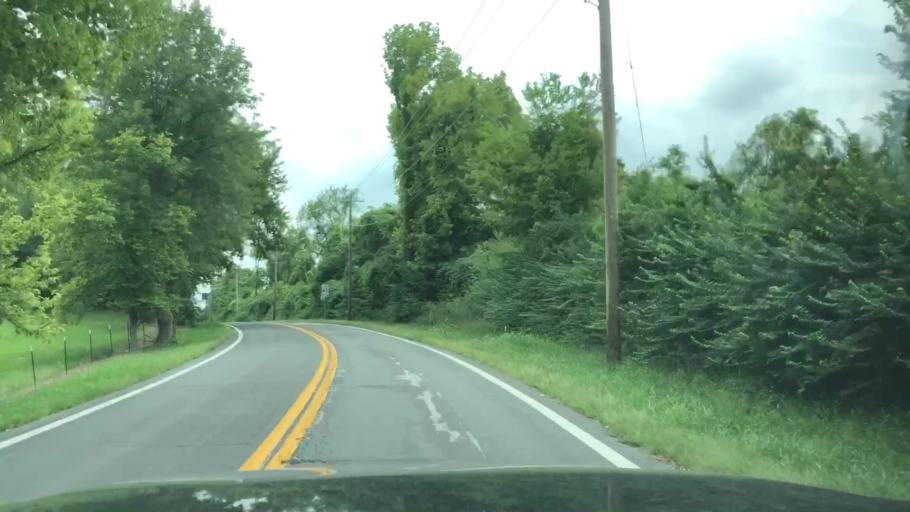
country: US
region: Missouri
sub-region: Saint Louis County
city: Hazelwood
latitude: 38.8135
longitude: -90.3787
